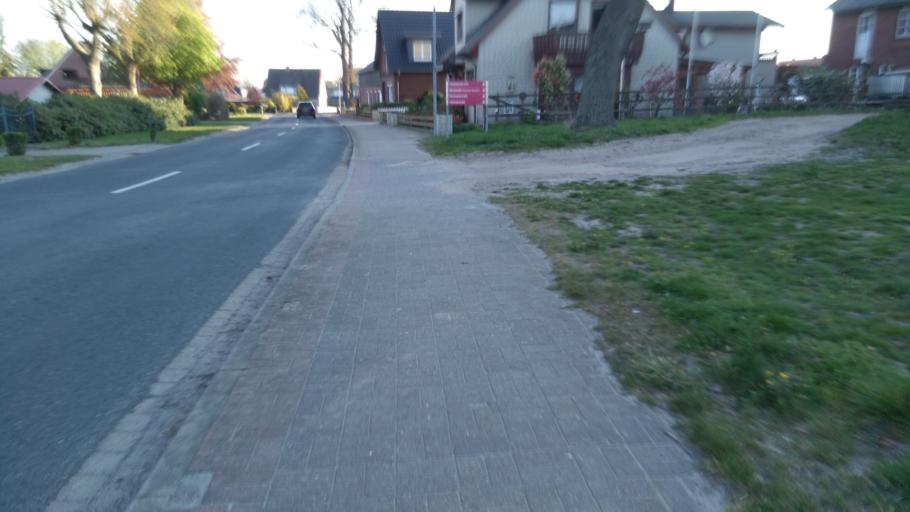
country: DE
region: Lower Saxony
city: Bliedersdorf
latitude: 53.4782
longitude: 9.5662
